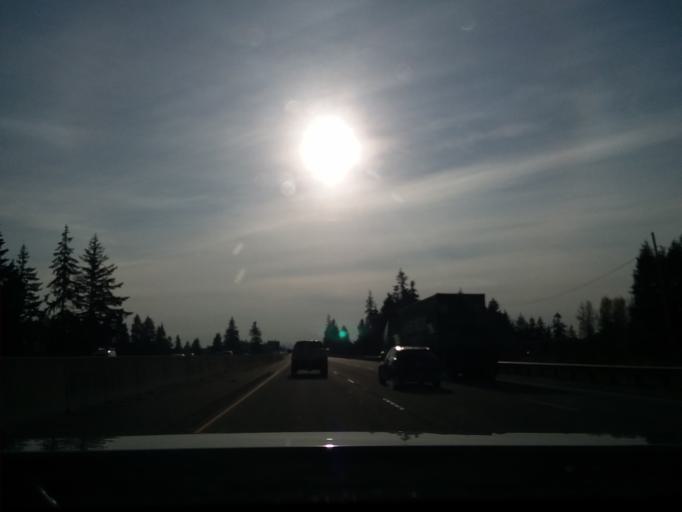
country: US
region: Washington
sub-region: Thurston County
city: Grand Mound
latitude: 46.8513
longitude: -122.9781
